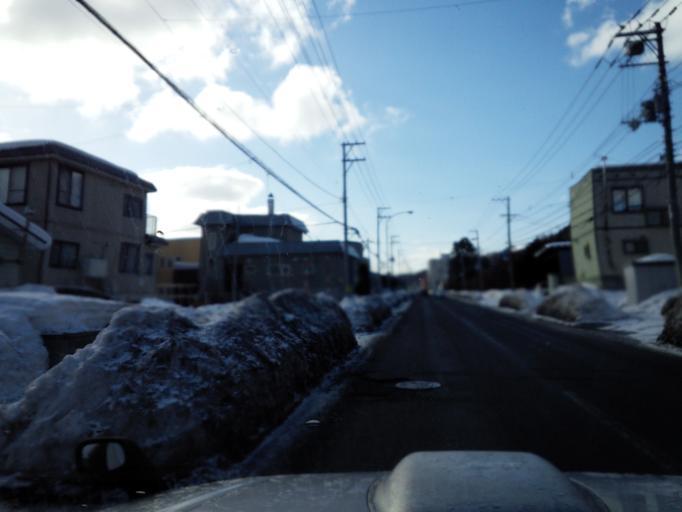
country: JP
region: Hokkaido
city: Sapporo
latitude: 42.9598
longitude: 141.3436
